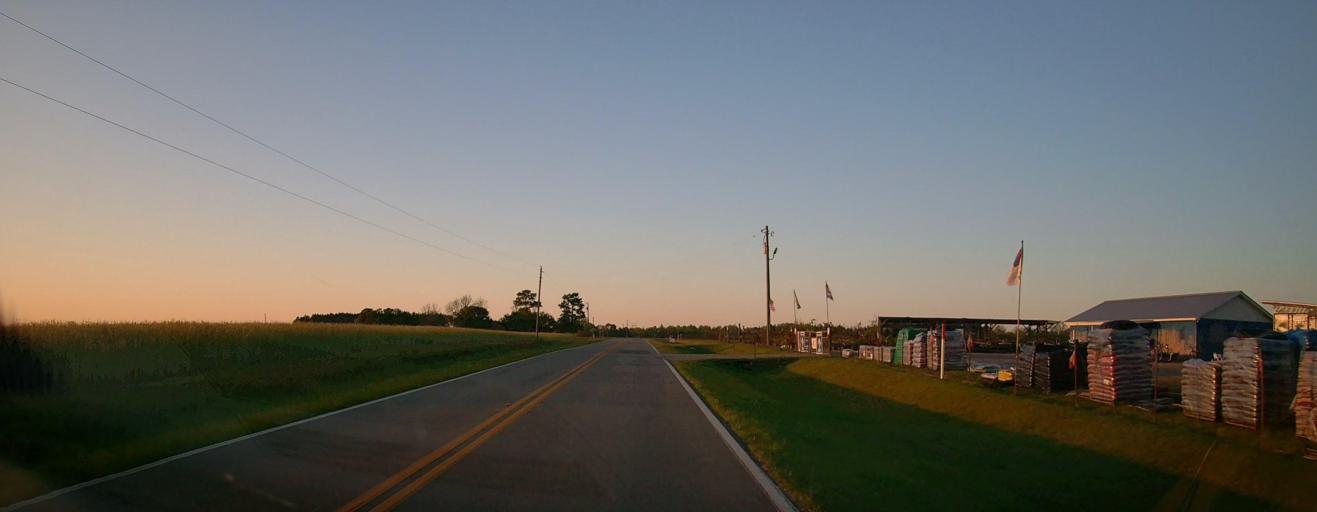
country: US
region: Georgia
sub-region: Ben Hill County
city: Fitzgerald
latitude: 31.7412
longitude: -83.3097
